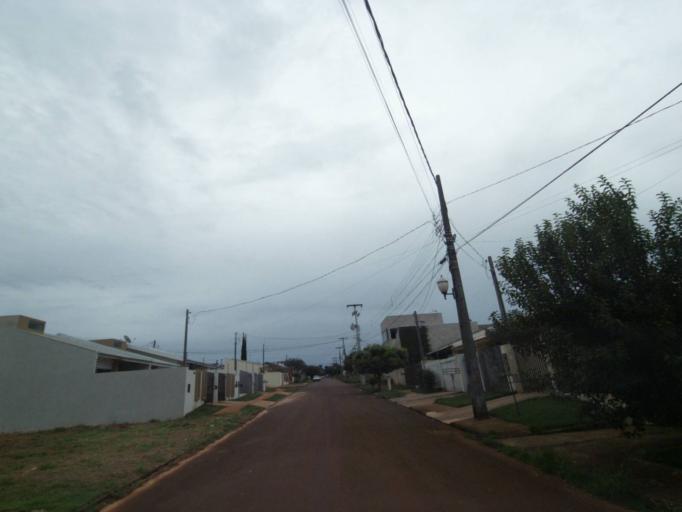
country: BR
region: Parana
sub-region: Campo Mourao
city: Campo Mourao
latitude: -24.0322
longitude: -52.3586
